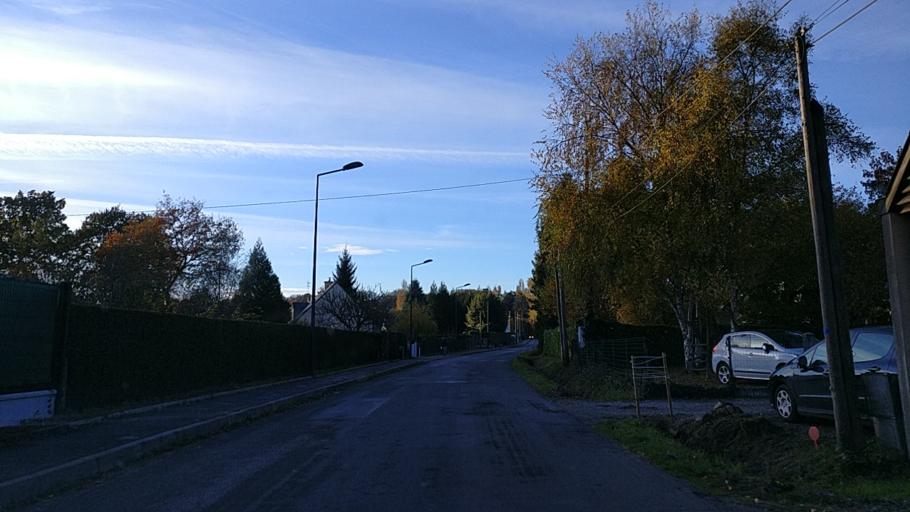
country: FR
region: Brittany
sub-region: Departement d'Ille-et-Vilaine
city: Liffre
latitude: 48.1881
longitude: -1.5197
